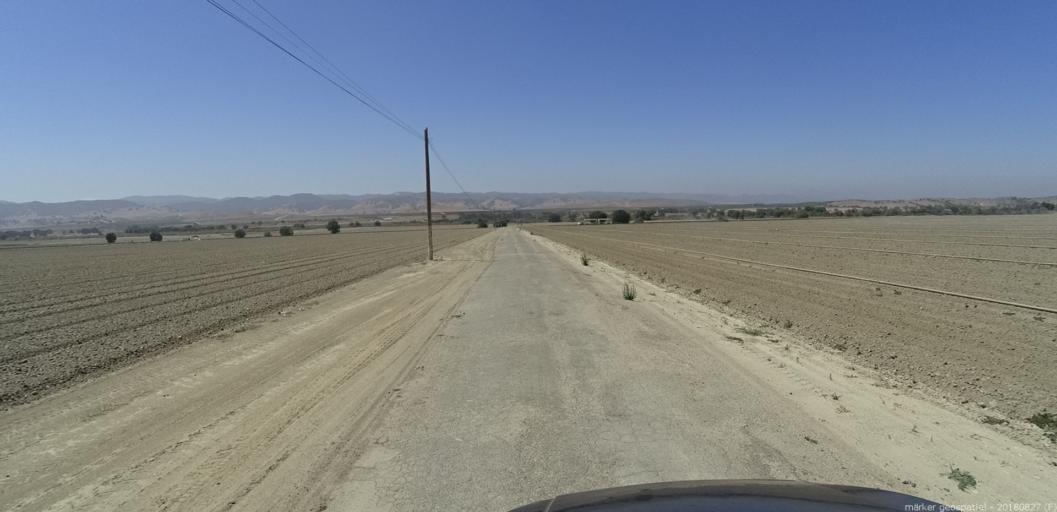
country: US
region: California
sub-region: Monterey County
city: King City
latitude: 36.0462
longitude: -120.9135
